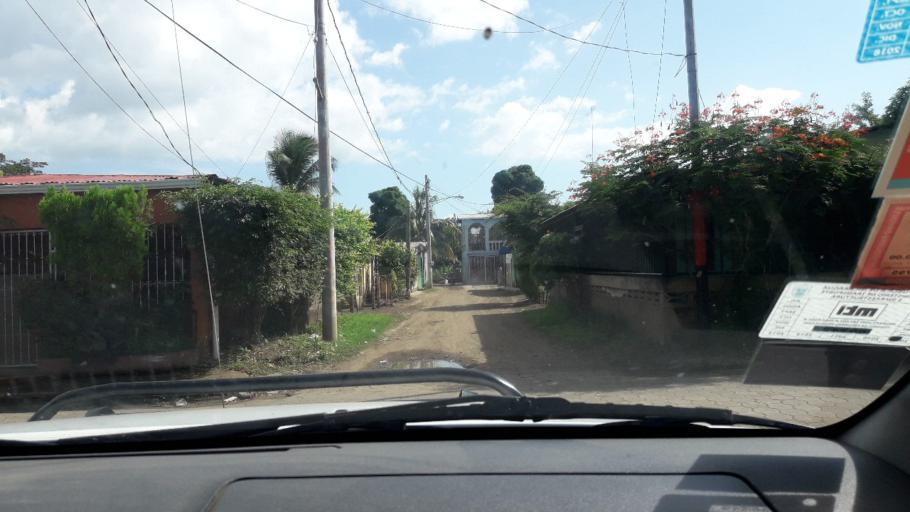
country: NI
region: Rivas
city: Rivas
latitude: 11.4493
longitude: -85.8213
